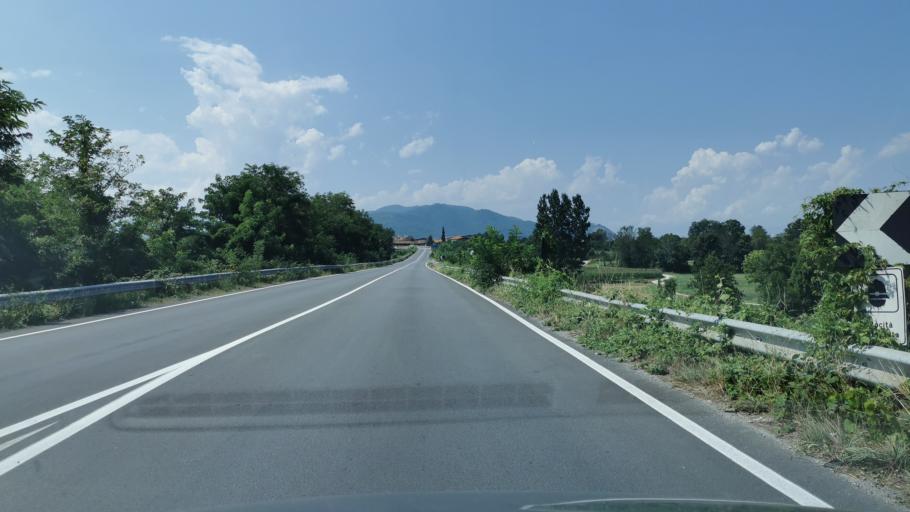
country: IT
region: Piedmont
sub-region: Provincia di Cuneo
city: Borgo San Dalmazzo
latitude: 44.3324
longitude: 7.5087
